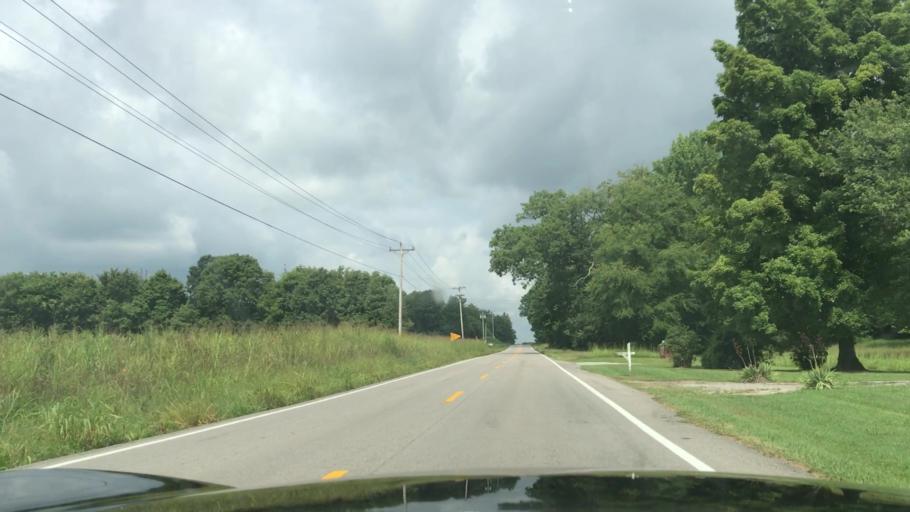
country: US
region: Kentucky
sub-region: Muhlenberg County
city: Central City
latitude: 37.1969
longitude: -86.9961
